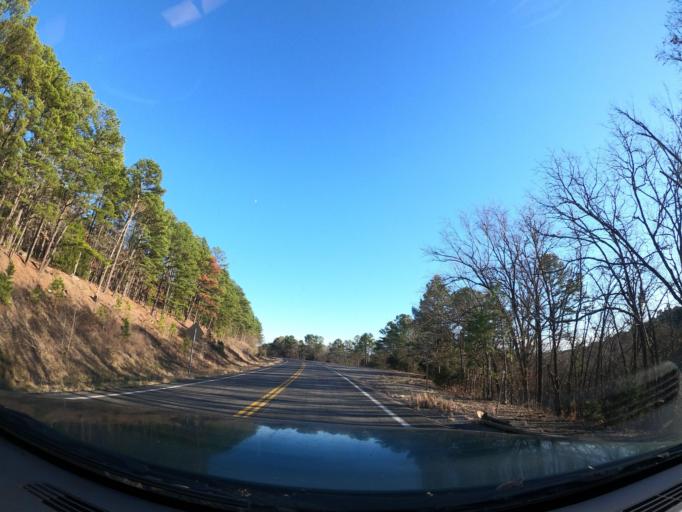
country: US
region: Oklahoma
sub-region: Latimer County
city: Wilburton
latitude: 34.9617
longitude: -95.3552
